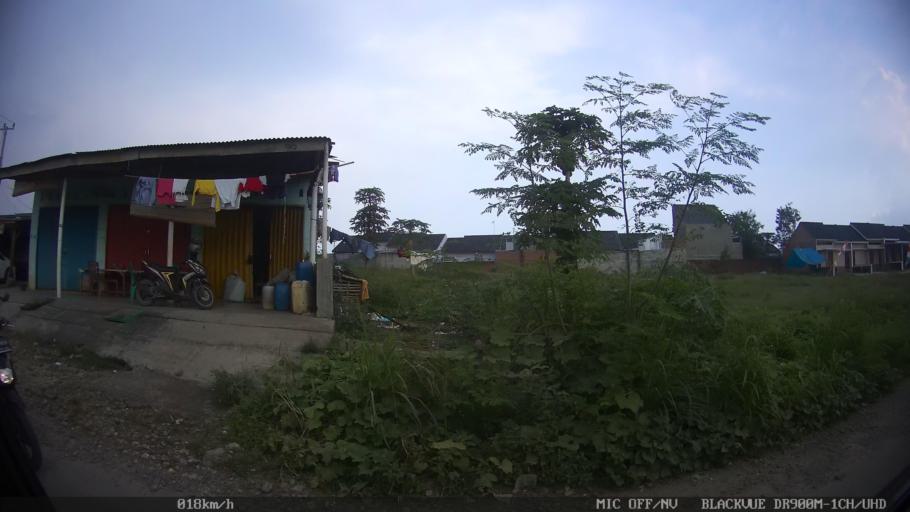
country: ID
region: Lampung
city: Kedaton
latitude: -5.3476
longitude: 105.2326
